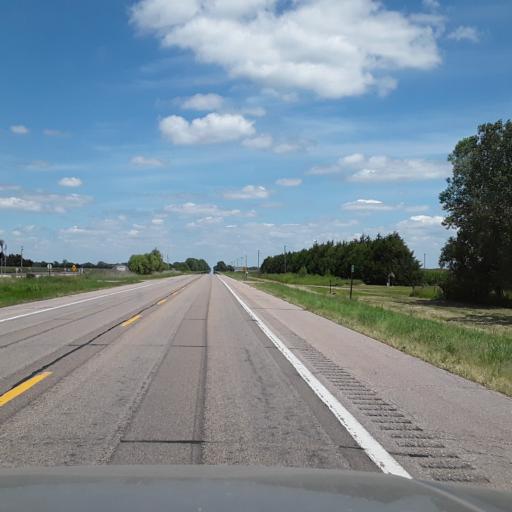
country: US
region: Nebraska
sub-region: Platte County
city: Columbus
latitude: 41.3704
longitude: -97.5355
